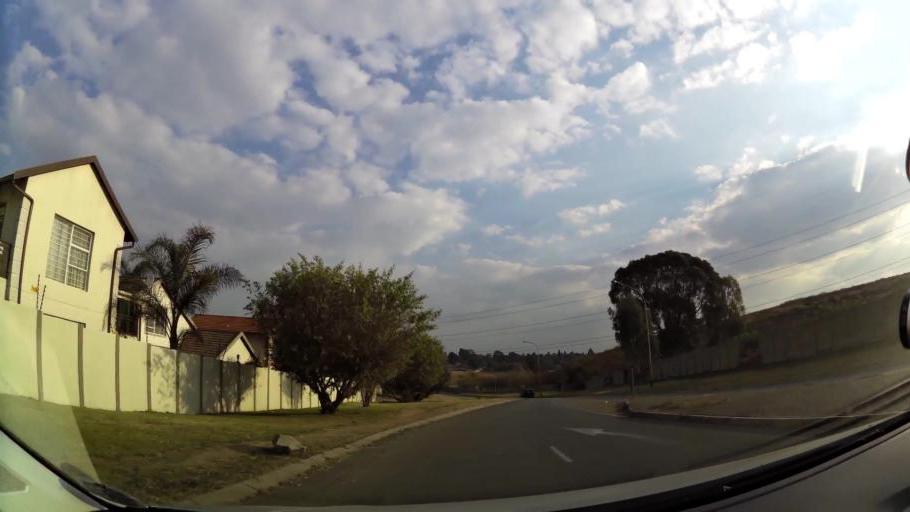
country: ZA
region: Gauteng
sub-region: City of Johannesburg Metropolitan Municipality
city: Modderfontein
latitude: -26.1297
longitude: 28.1855
